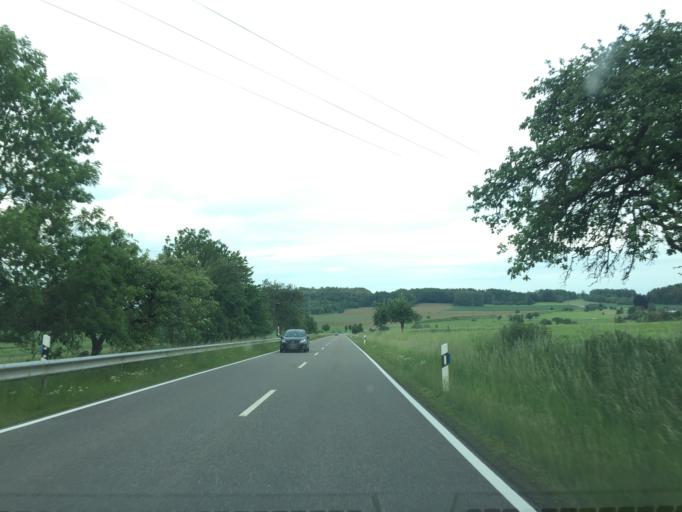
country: DE
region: Rheinland-Pfalz
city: Weroth
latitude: 50.4548
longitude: 7.9536
